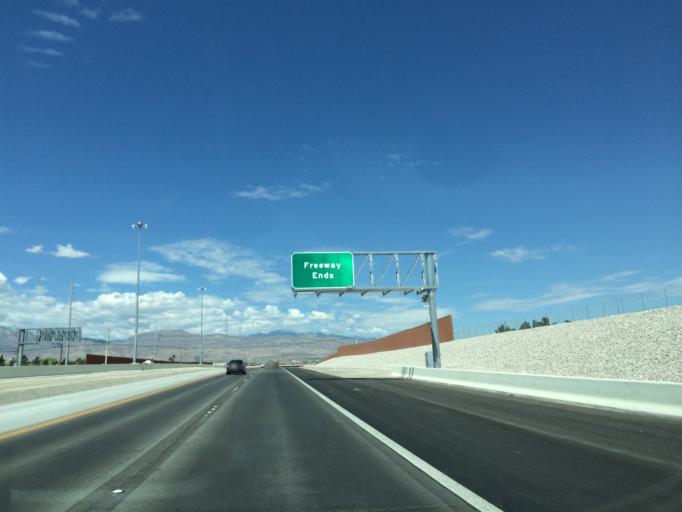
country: US
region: Nevada
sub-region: Clark County
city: Las Vegas
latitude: 36.2756
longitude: -115.2442
